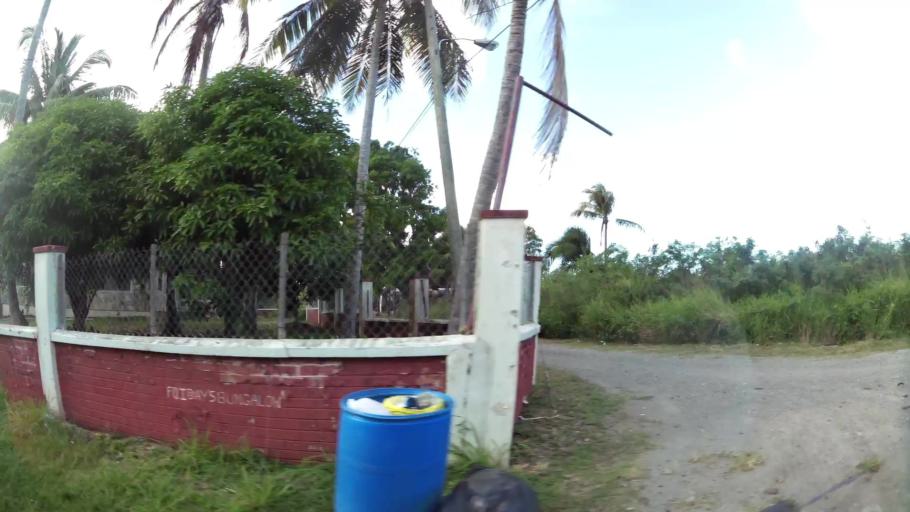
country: AG
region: Saint Peter
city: All Saints
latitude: 17.0744
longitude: -61.7854
